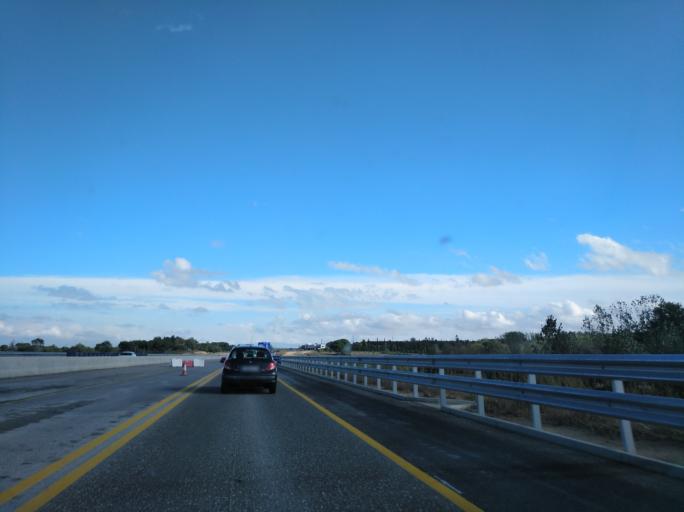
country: ES
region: Catalonia
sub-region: Provincia de Girona
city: Sils
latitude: 41.7933
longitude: 2.7583
